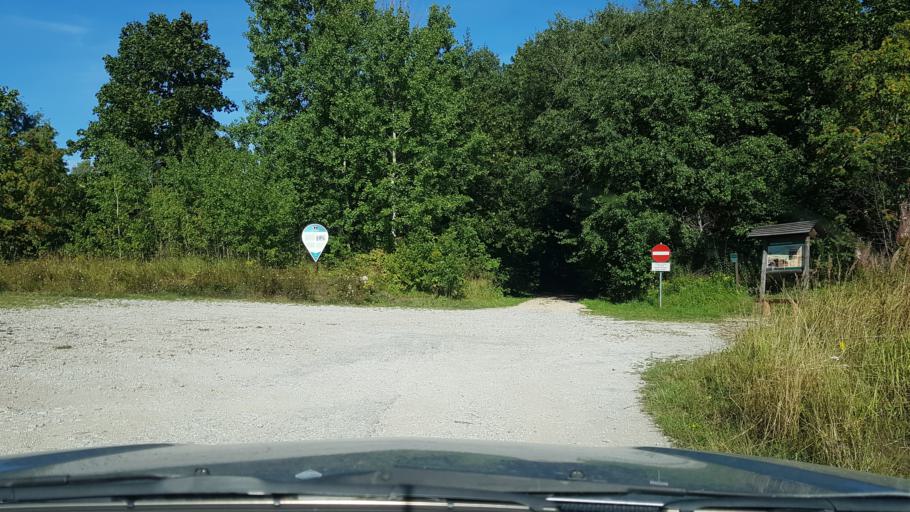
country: EE
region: Ida-Virumaa
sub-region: Sillamaee linn
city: Sillamae
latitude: 59.3956
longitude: 27.8777
